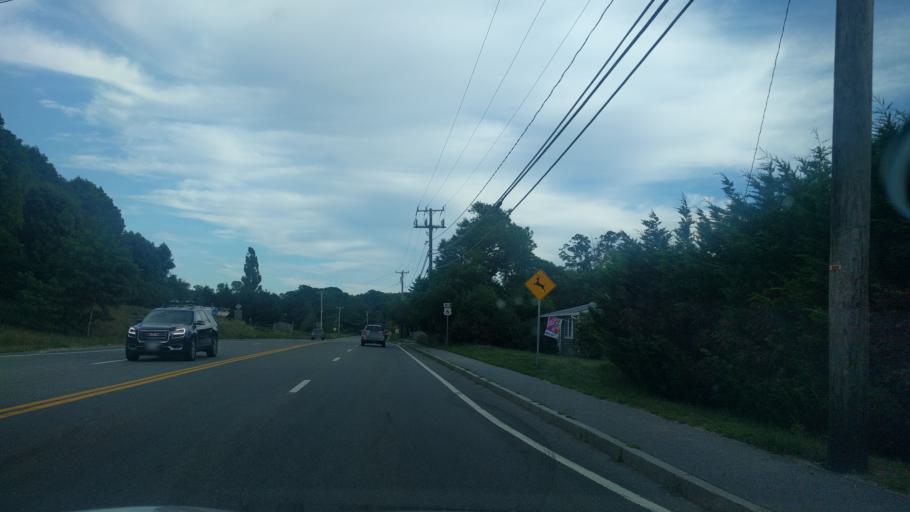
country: US
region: Massachusetts
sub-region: Barnstable County
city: Eastham
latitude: 41.8191
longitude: -69.9693
